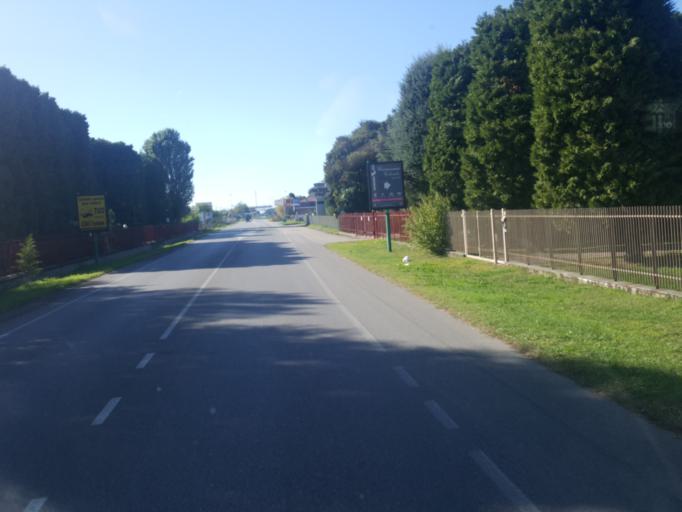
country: IT
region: Lombardy
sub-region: Citta metropolitana di Milano
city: Vittuone
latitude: 45.4822
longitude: 8.9624
